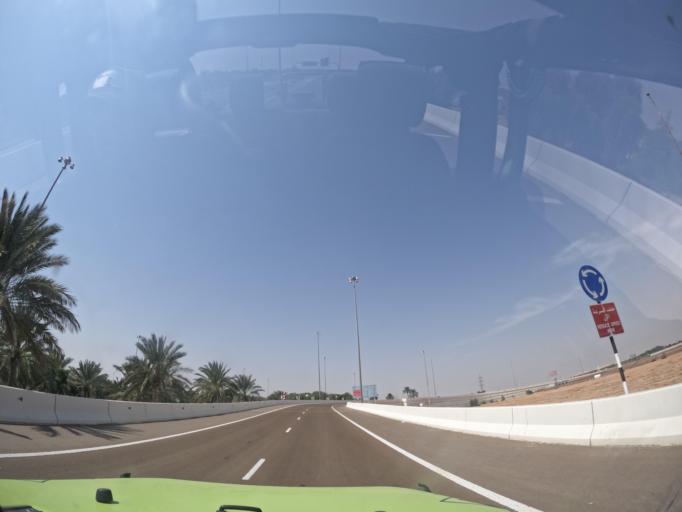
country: AE
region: Abu Dhabi
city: Al Ain
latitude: 24.1781
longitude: 55.1358
